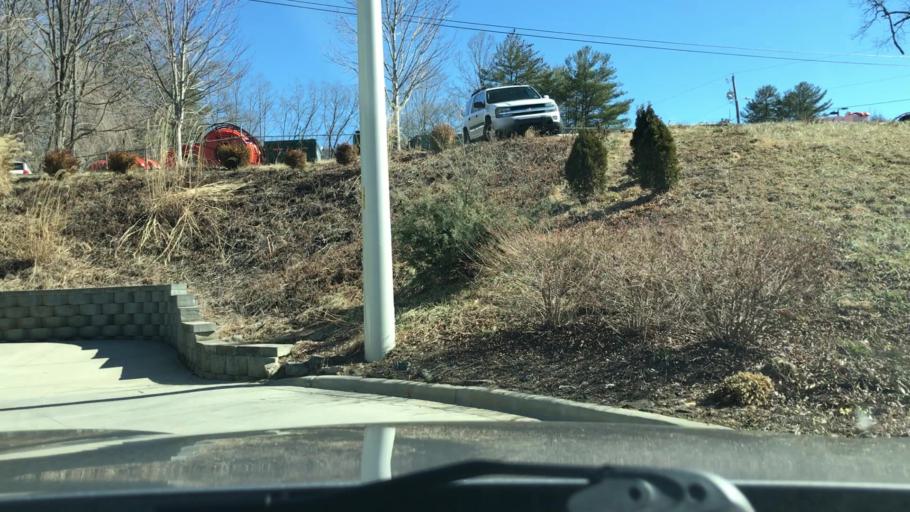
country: US
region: North Carolina
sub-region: Buncombe County
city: Royal Pines
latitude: 35.4857
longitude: -82.5248
